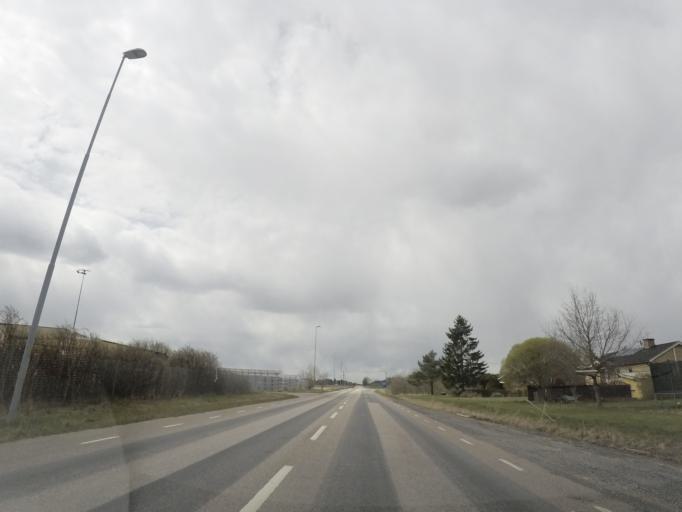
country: SE
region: Soedermanland
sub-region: Nykopings Kommun
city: Stigtomta
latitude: 58.7441
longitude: 16.7152
